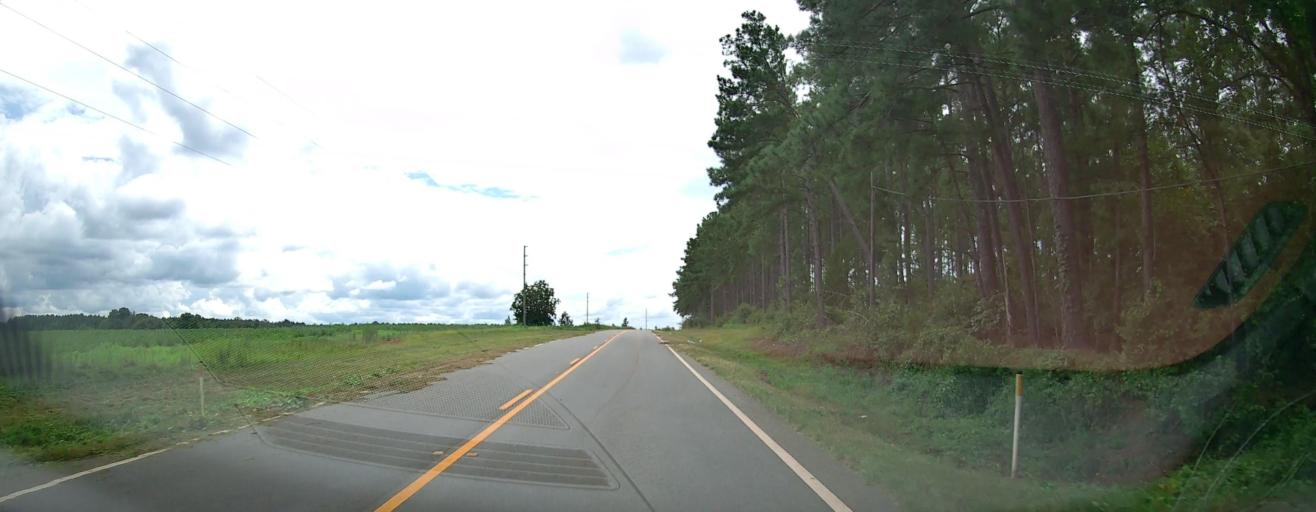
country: US
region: Georgia
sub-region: Macon County
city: Oglethorpe
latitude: 32.2701
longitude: -84.1846
